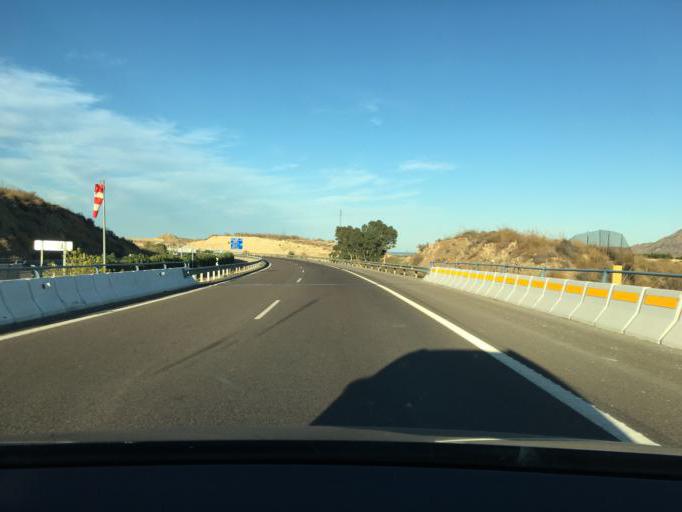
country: ES
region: Andalusia
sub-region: Provincia de Almeria
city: Bedar
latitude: 37.1454
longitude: -1.9635
